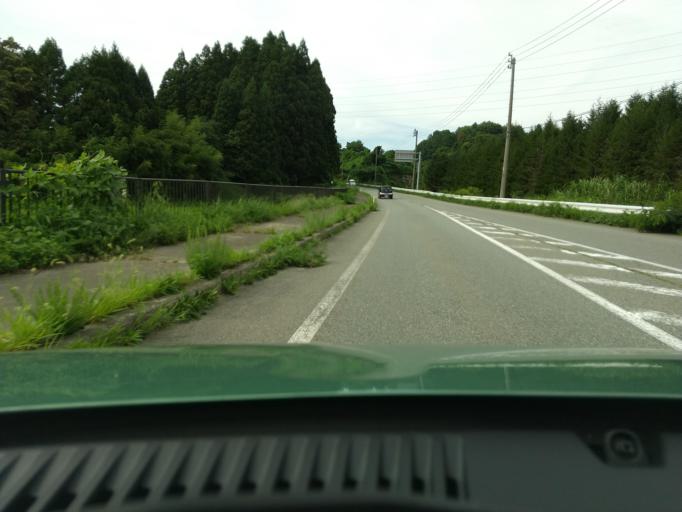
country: JP
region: Akita
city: Akita Shi
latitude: 39.8060
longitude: 140.0947
